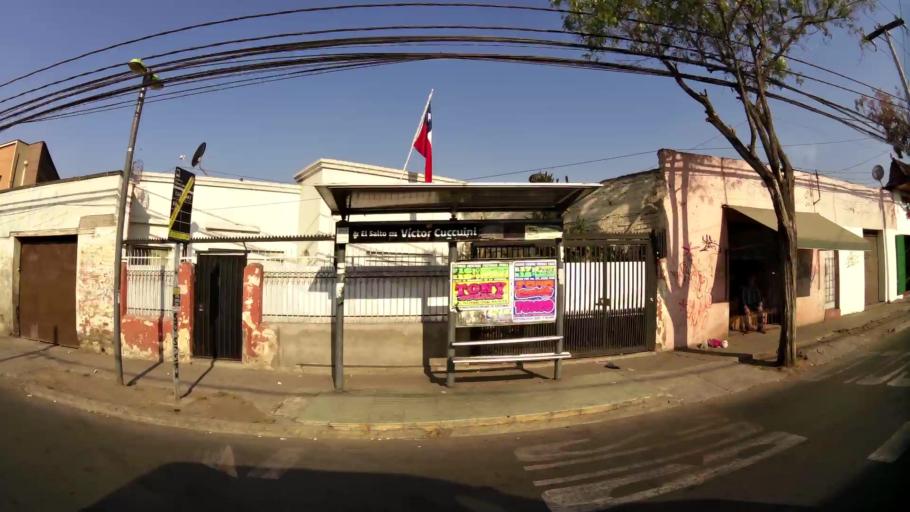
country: CL
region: Santiago Metropolitan
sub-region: Provincia de Santiago
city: Santiago
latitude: -33.4043
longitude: -70.6322
